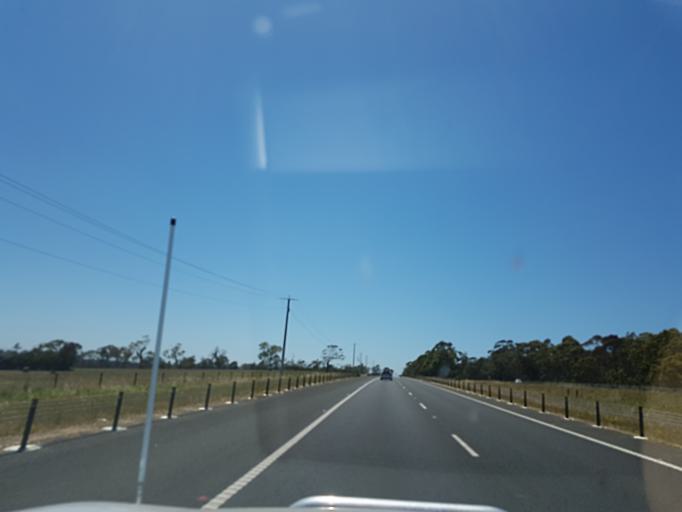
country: AU
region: Victoria
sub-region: Latrobe
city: Traralgon
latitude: -38.1688
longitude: 146.6874
